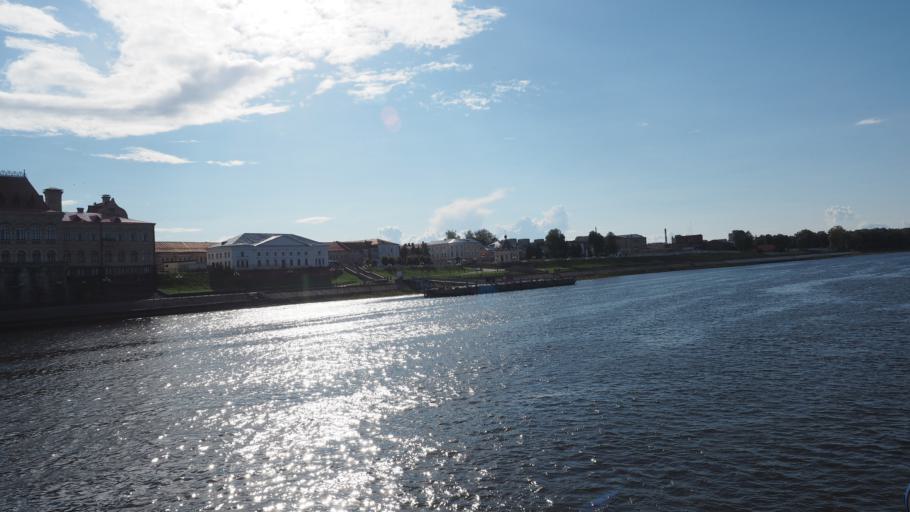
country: RU
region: Jaroslavl
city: Rybinsk
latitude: 58.0509
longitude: 38.8592
